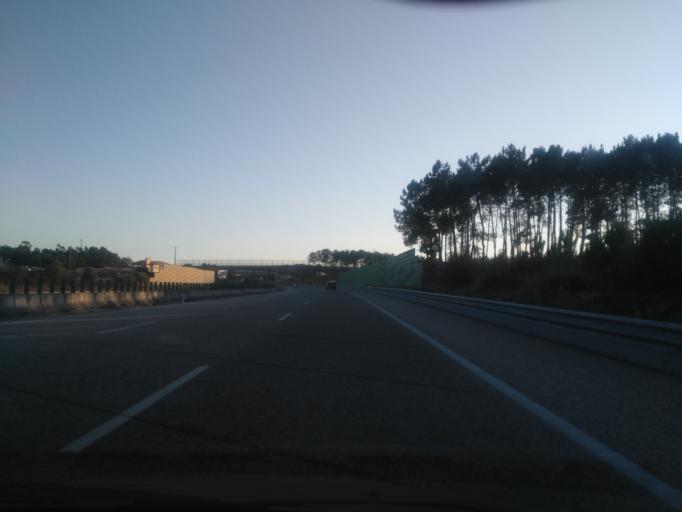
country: PT
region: Leiria
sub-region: Leiria
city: Monte Redondo
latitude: 39.9335
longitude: -8.7758
